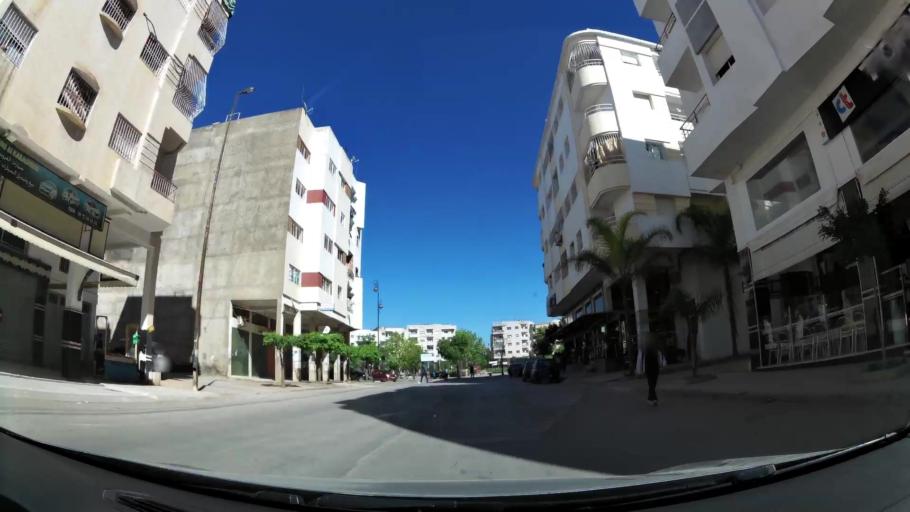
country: MA
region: Fes-Boulemane
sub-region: Fes
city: Fes
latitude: 34.0162
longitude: -4.9766
